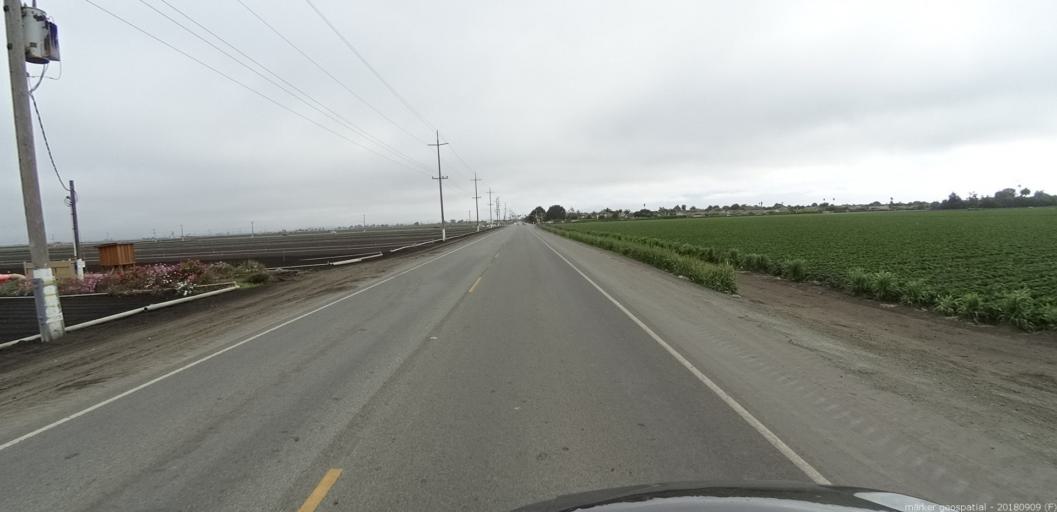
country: US
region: California
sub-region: Monterey County
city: Salinas
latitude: 36.6639
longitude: -121.6876
